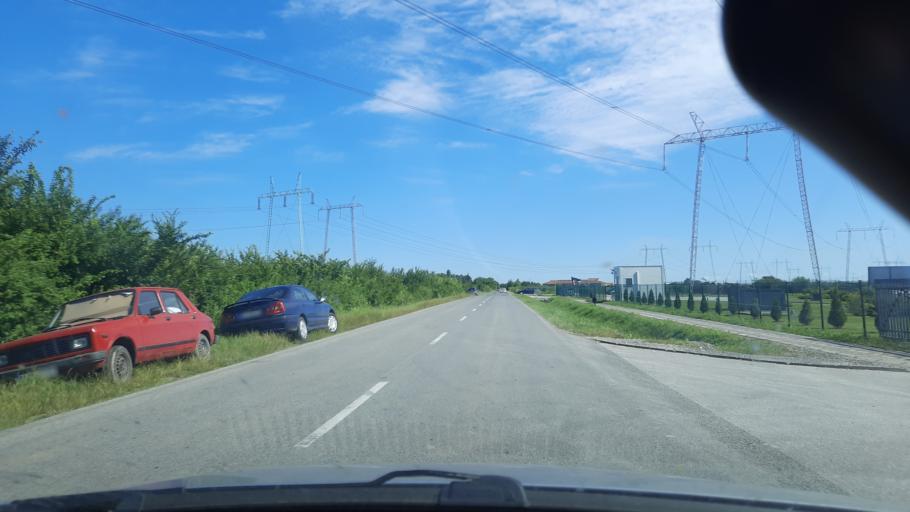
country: RS
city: Simanovci
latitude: 44.8497
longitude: 20.1014
